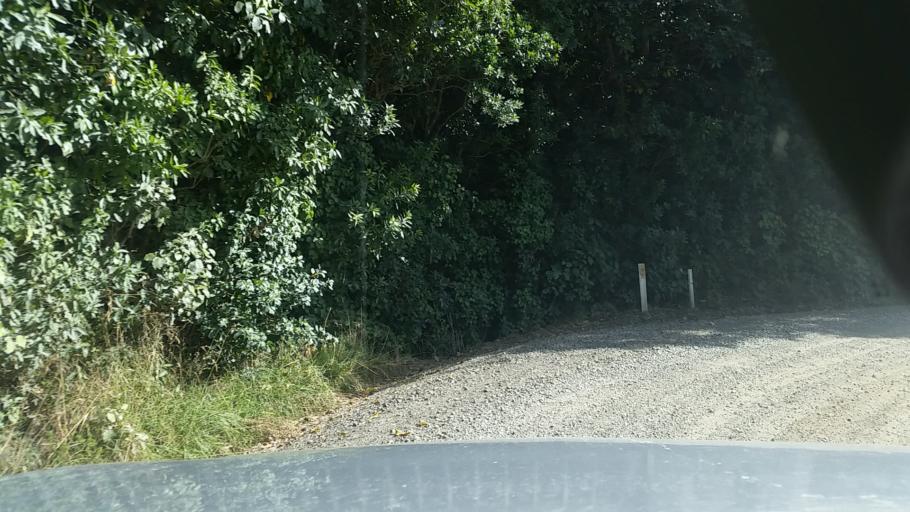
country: NZ
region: Marlborough
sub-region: Marlborough District
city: Picton
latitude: -41.2895
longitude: 174.1290
